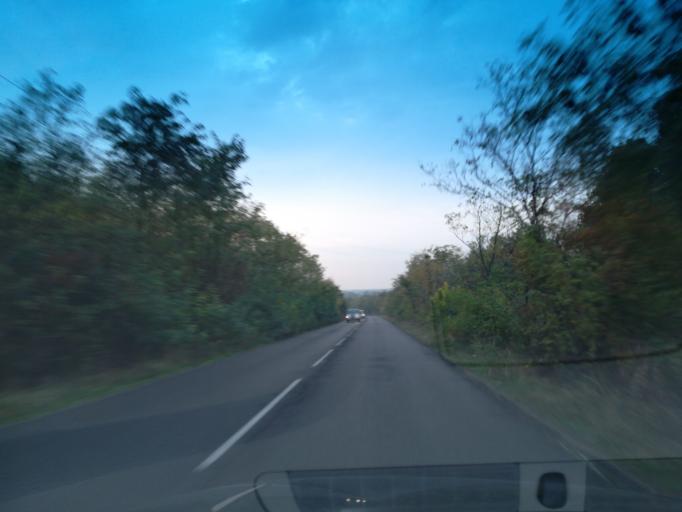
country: BG
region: Stara Zagora
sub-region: Obshtina Chirpan
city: Chirpan
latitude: 42.1796
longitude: 25.2247
